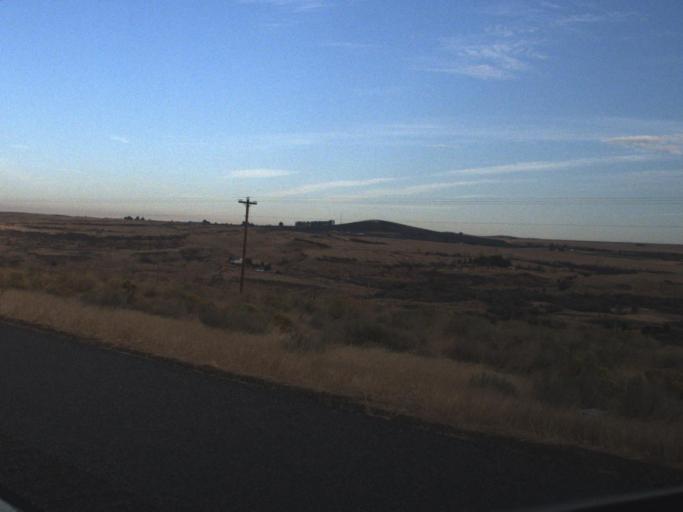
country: US
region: Washington
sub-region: Benton County
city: Benton City
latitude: 46.2677
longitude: -119.5596
